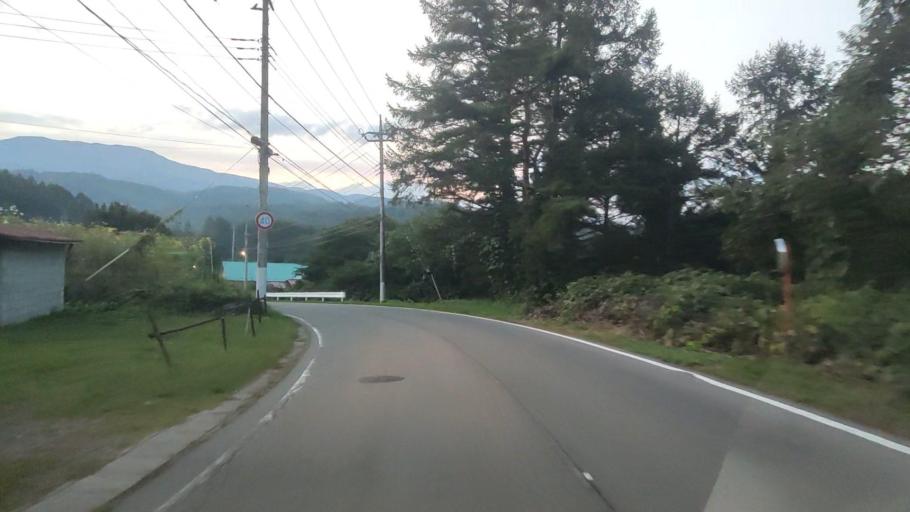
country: JP
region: Gunma
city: Nakanojomachi
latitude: 36.5418
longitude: 138.6029
